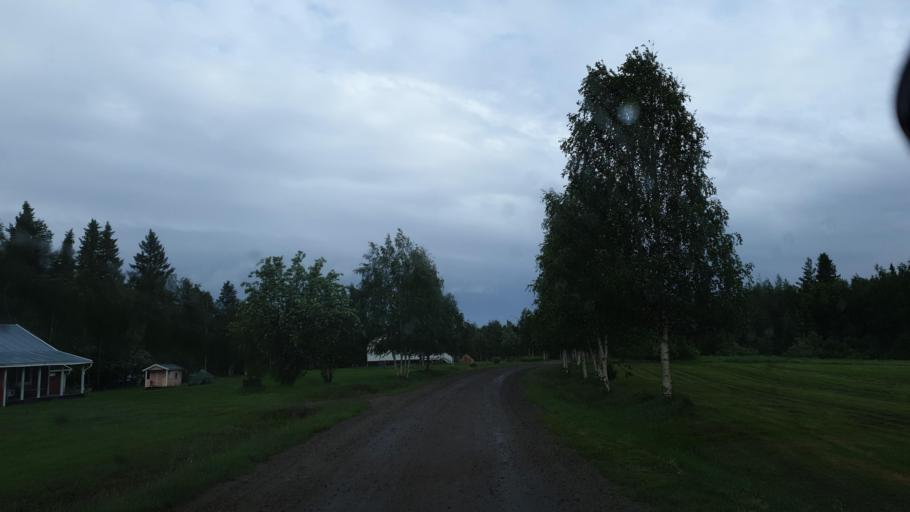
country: SE
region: Norrbotten
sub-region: Arvidsjaurs Kommun
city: Arvidsjaur
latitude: 65.7073
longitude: 18.7113
